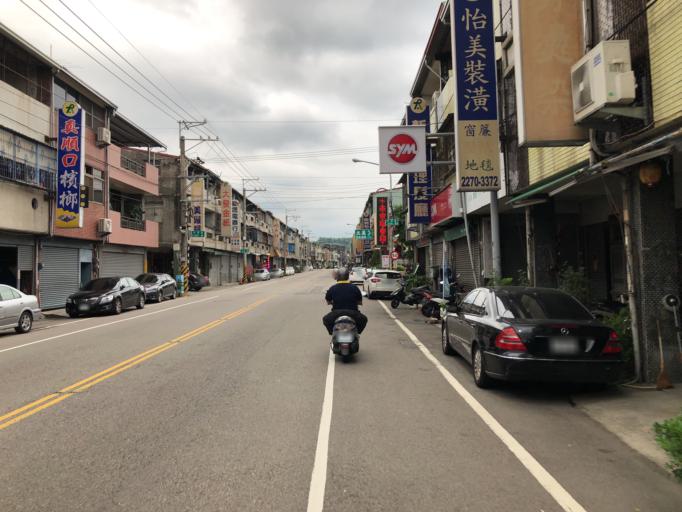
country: TW
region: Taiwan
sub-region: Taichung City
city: Taichung
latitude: 24.1236
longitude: 120.7346
